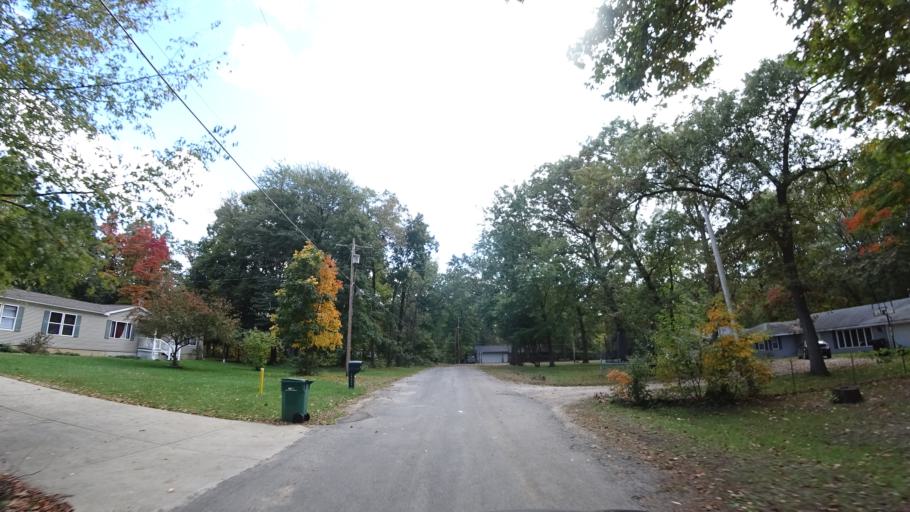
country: US
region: Michigan
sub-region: Saint Joseph County
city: Three Rivers
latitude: 41.9538
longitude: -85.5869
